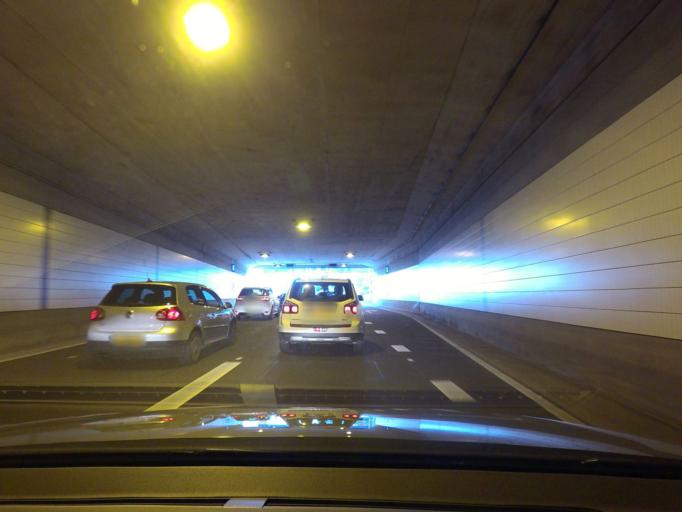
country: NL
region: South Holland
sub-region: Gemeente Leidschendam-Voorburg
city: Voorburg
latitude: 52.0859
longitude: 4.3785
